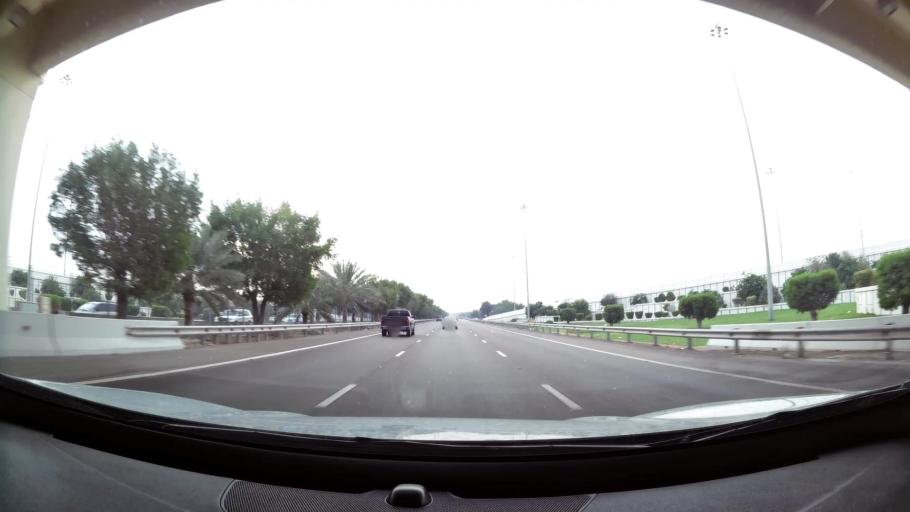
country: AE
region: Abu Dhabi
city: Abu Dhabi
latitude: 24.2807
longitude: 54.6480
